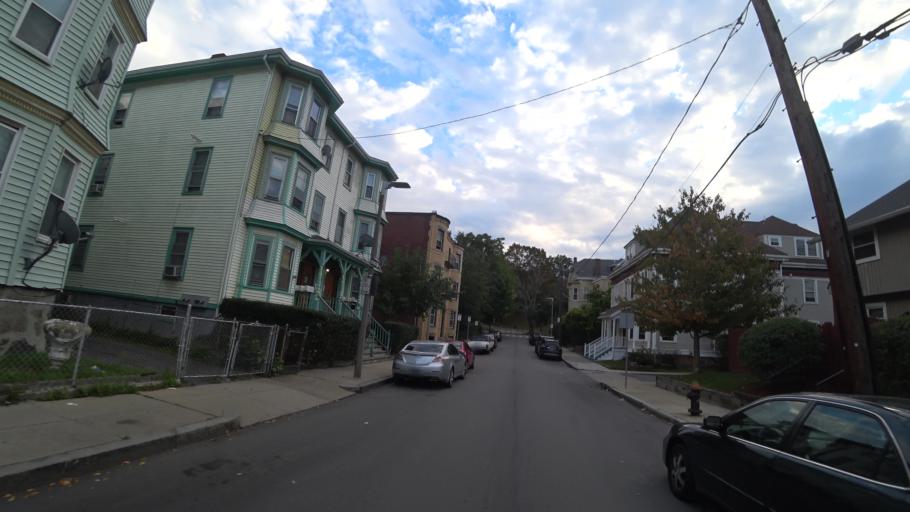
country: US
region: Massachusetts
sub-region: Norfolk County
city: Brookline
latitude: 42.3227
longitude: -71.0871
